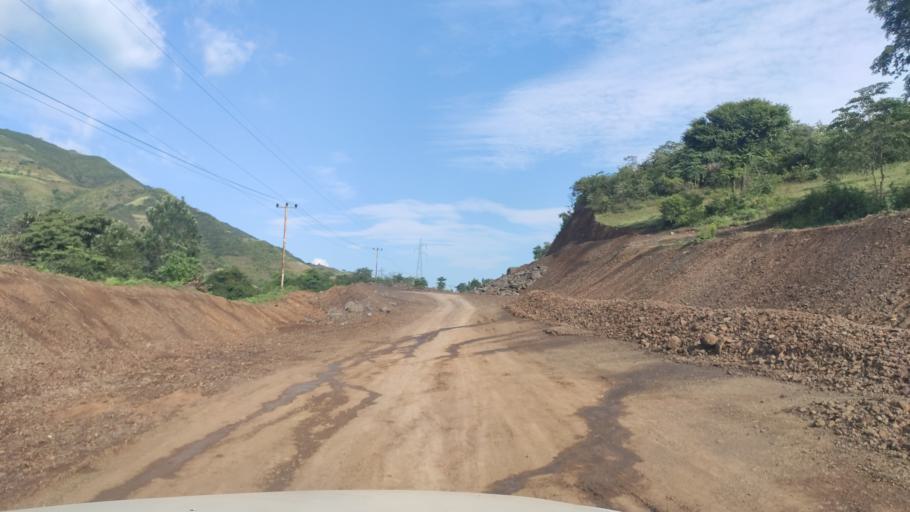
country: ET
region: Southern Nations, Nationalities, and People's Region
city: Arba Minch'
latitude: 6.4257
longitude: 37.3413
